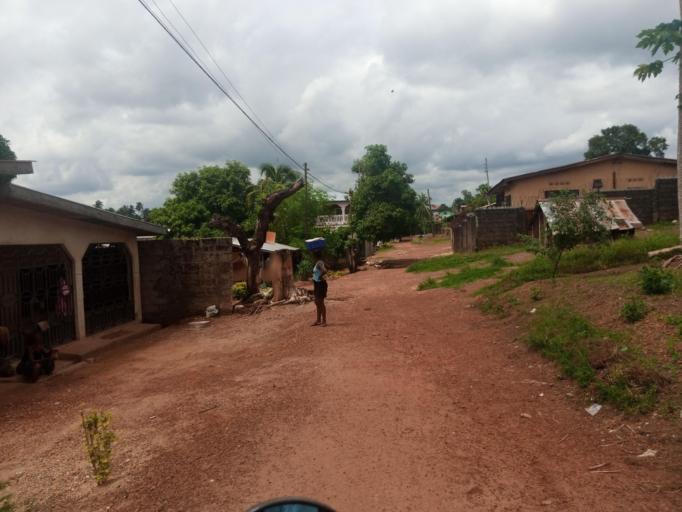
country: SL
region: Southern Province
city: Bo
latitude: 7.9559
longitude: -11.7376
